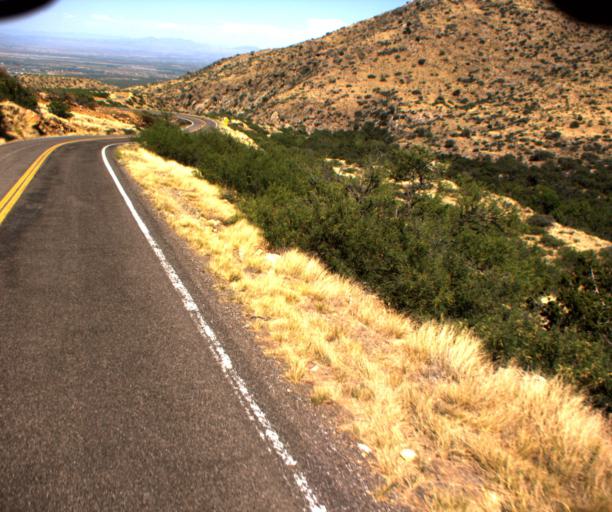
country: US
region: Arizona
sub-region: Graham County
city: Swift Trail Junction
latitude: 32.6754
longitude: -109.7794
